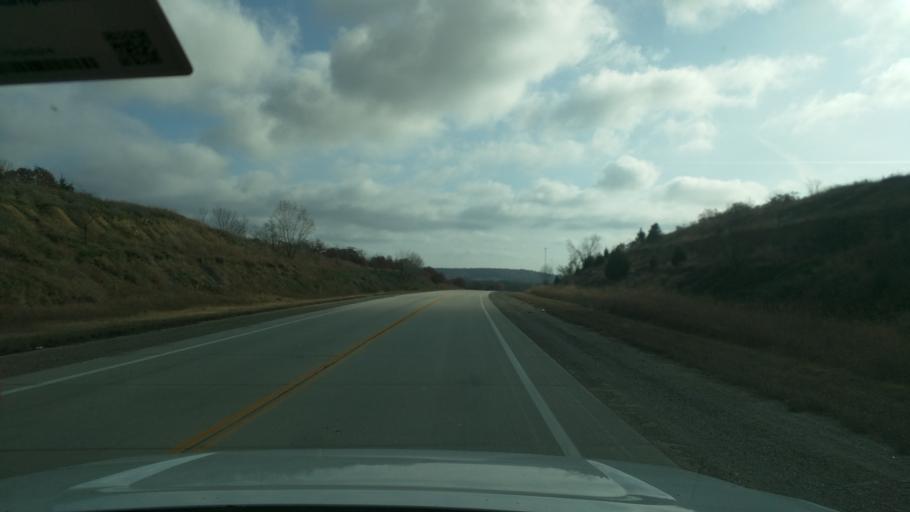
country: US
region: Kansas
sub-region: Chautauqua County
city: Sedan
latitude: 37.0820
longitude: -96.1143
